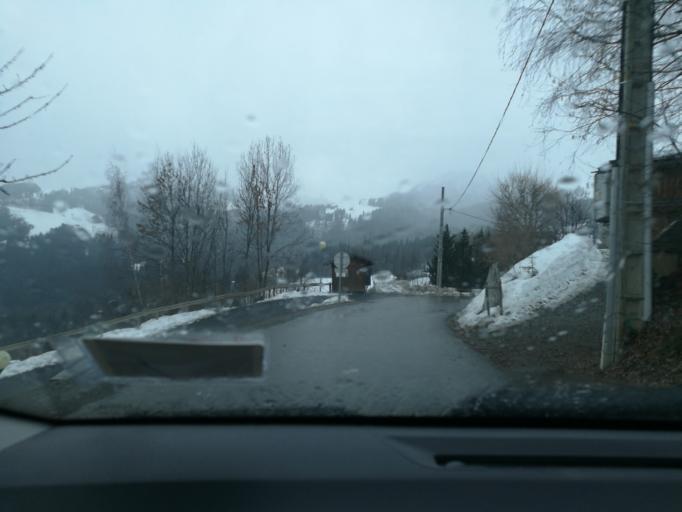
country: FR
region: Rhone-Alpes
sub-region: Departement de la Haute-Savoie
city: Saint-Gervais-les-Bains
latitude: 45.8714
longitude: 6.6898
